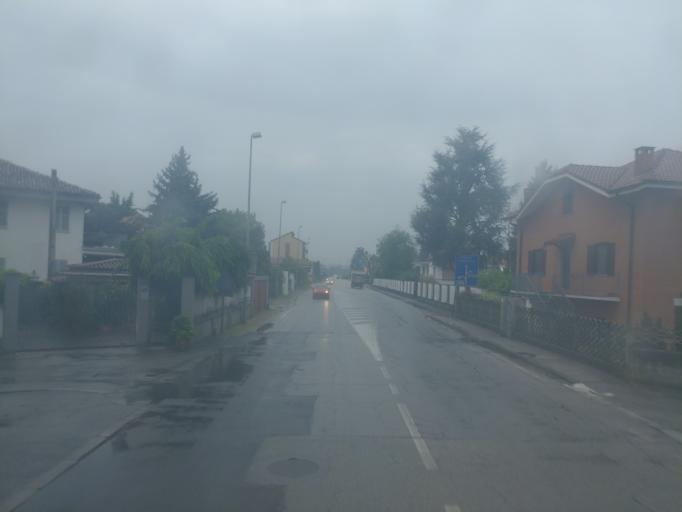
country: IT
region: Piedmont
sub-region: Provincia di Torino
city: La Loggia
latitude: 44.9595
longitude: 7.6675
